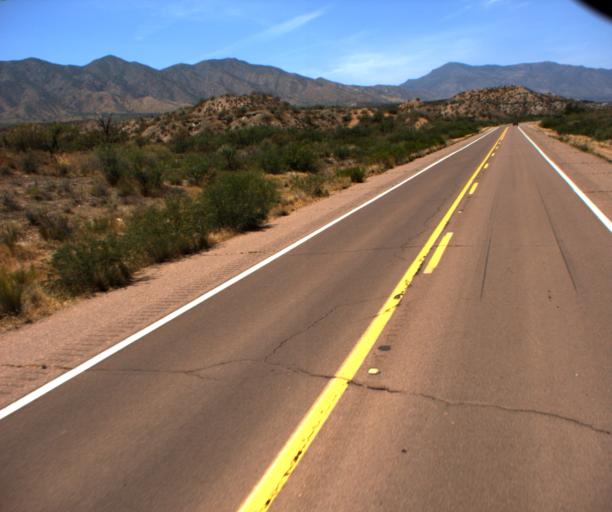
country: US
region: Arizona
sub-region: Gila County
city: Tonto Basin
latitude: 33.8200
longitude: -111.2901
